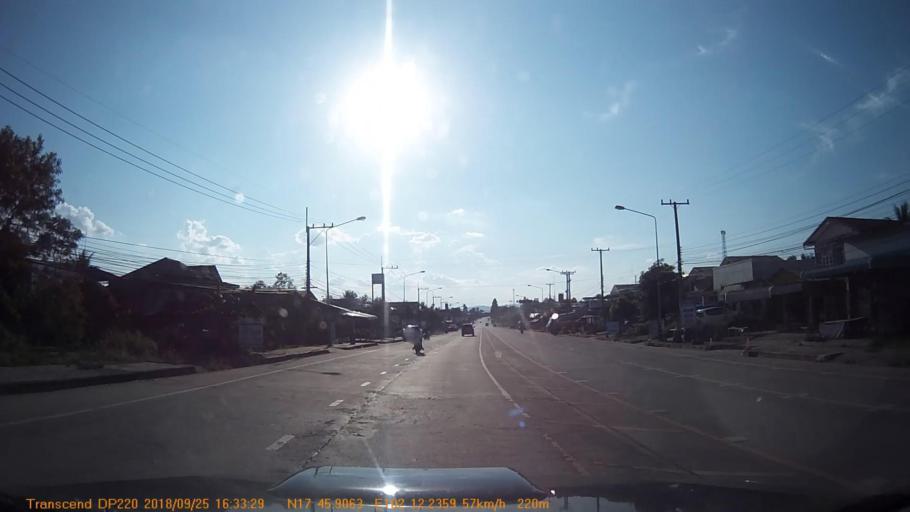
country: TH
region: Changwat Udon Thani
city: Nam Som
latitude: 17.7651
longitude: 102.2039
